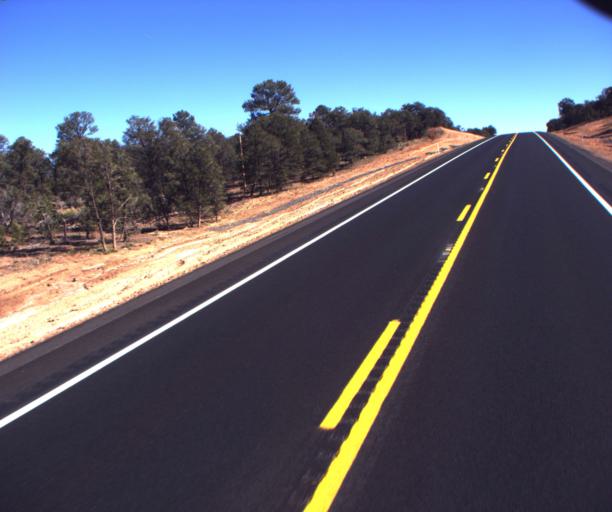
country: US
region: Arizona
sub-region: Apache County
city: Ganado
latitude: 35.7146
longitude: -109.3379
